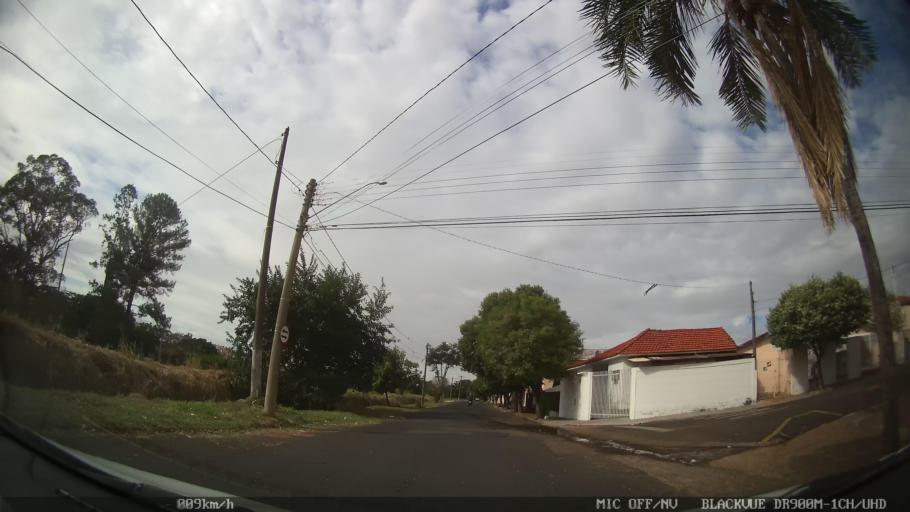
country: BR
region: Sao Paulo
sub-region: Sao Jose Do Rio Preto
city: Sao Jose do Rio Preto
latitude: -20.8153
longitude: -49.3519
